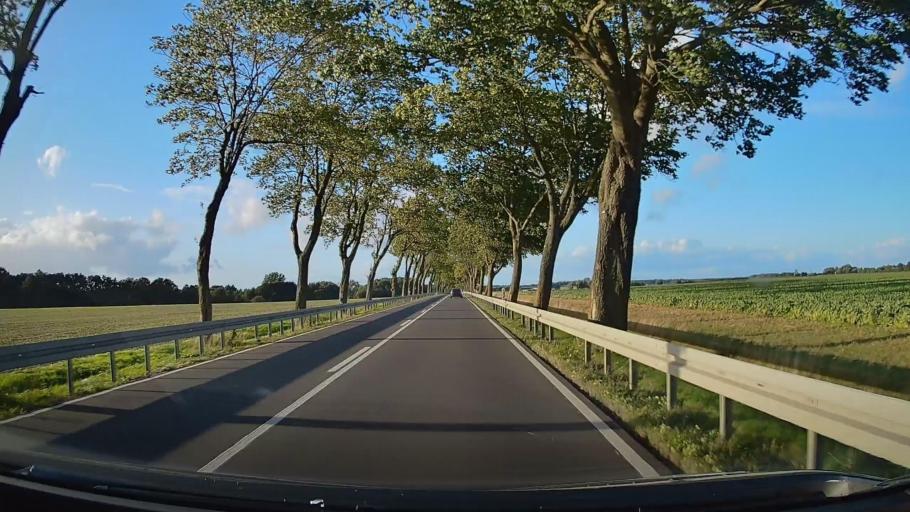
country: DE
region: Mecklenburg-Vorpommern
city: Steinhagen
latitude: 54.2158
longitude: 13.0048
